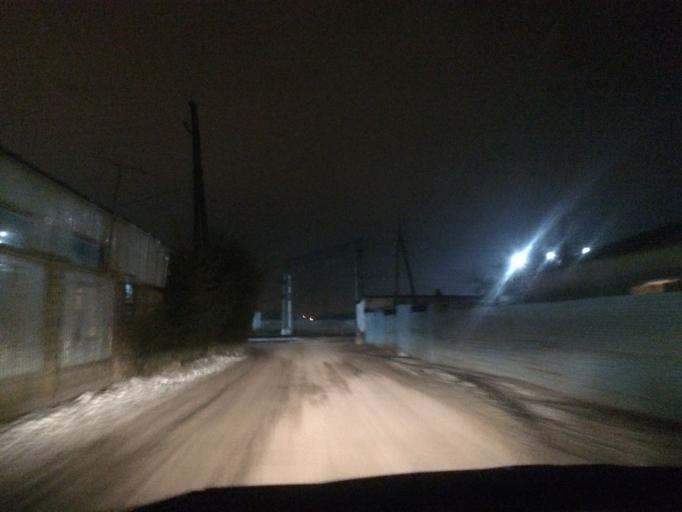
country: KZ
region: Astana Qalasy
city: Astana
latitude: 51.2084
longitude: 71.3895
